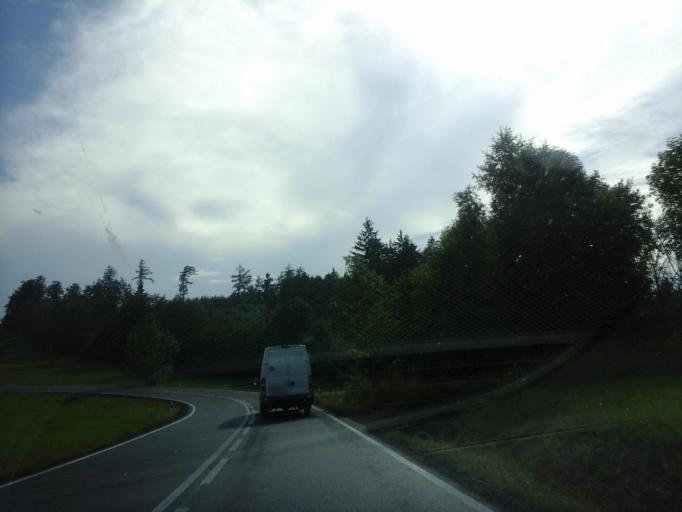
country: CZ
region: Olomoucky
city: Stity
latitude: 49.9505
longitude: 16.6874
